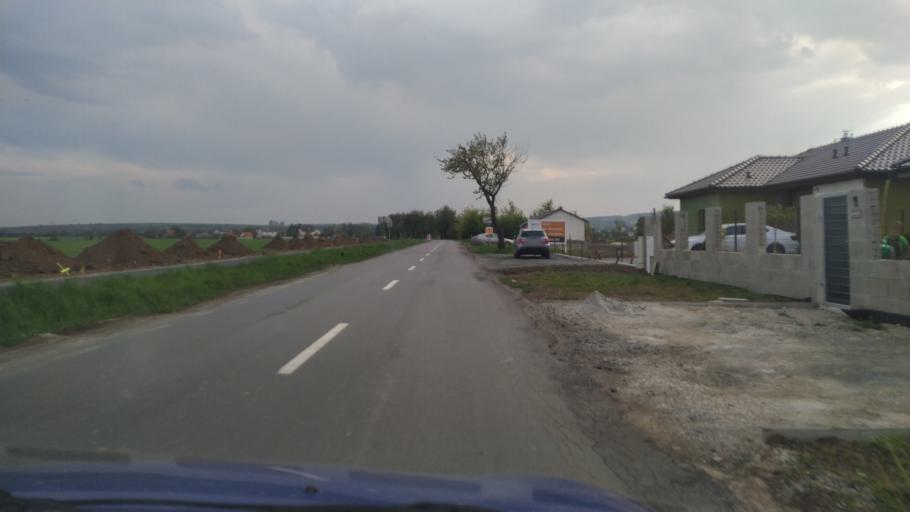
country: CZ
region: Olomoucky
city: Lutin
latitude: 49.5549
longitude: 17.1293
